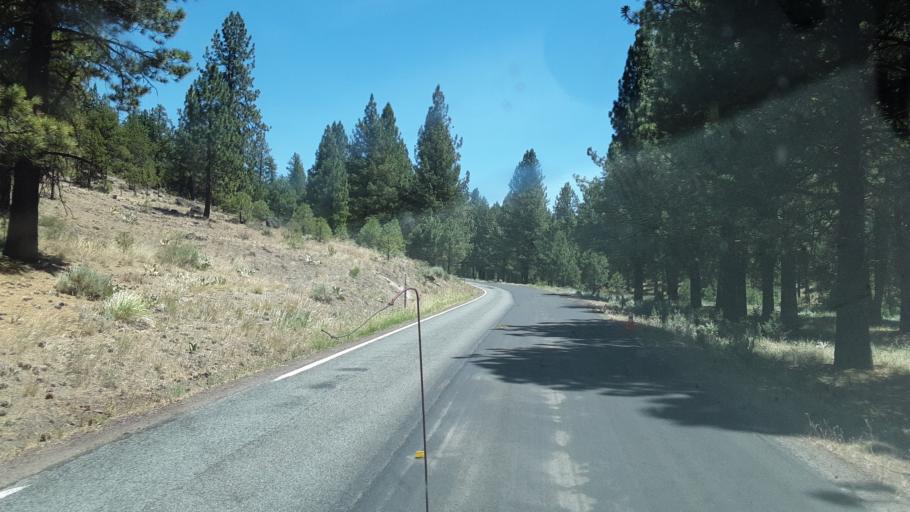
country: US
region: California
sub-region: Modoc County
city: Alturas
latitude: 41.0124
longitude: -120.8216
